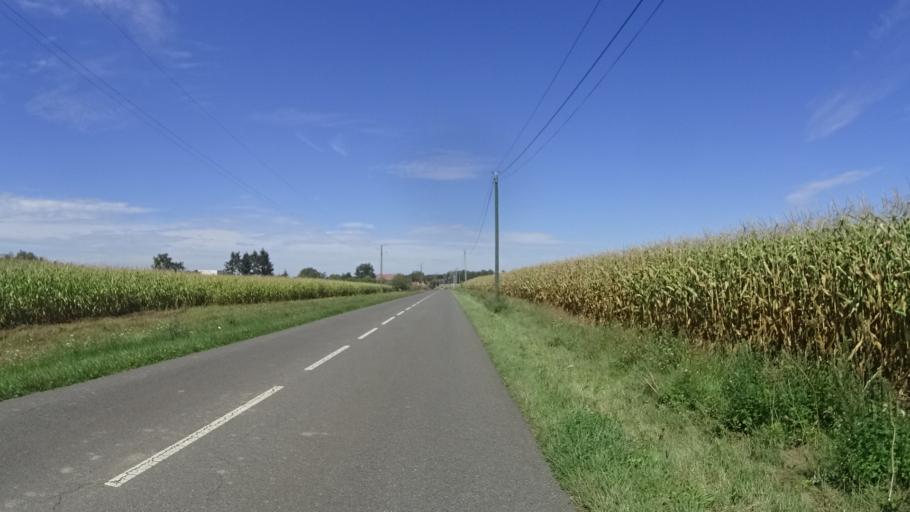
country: FR
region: Centre
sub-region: Departement du Loiret
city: Briare
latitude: 47.6205
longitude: 2.7523
